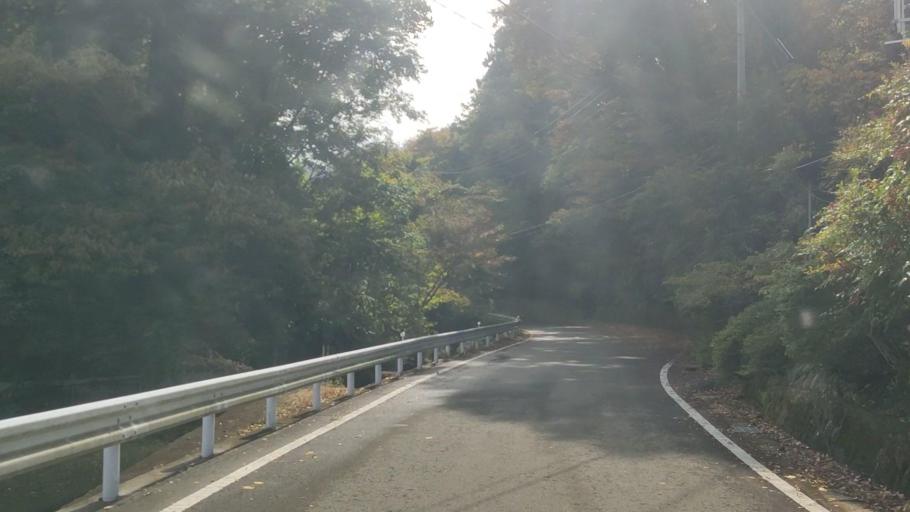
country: JP
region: Yamanashi
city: Ryuo
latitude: 35.4483
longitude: 138.4490
